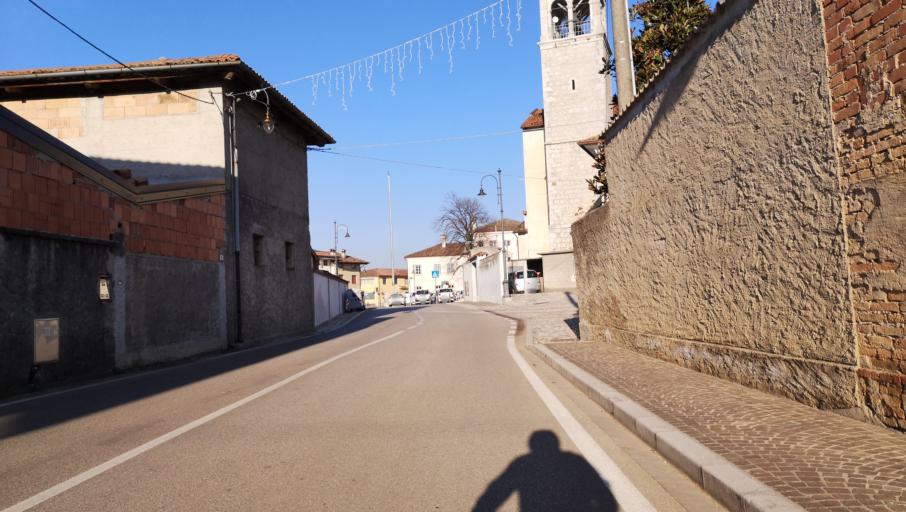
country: IT
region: Friuli Venezia Giulia
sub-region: Provincia di Udine
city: Bicinicco
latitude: 45.9543
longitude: 13.2687
